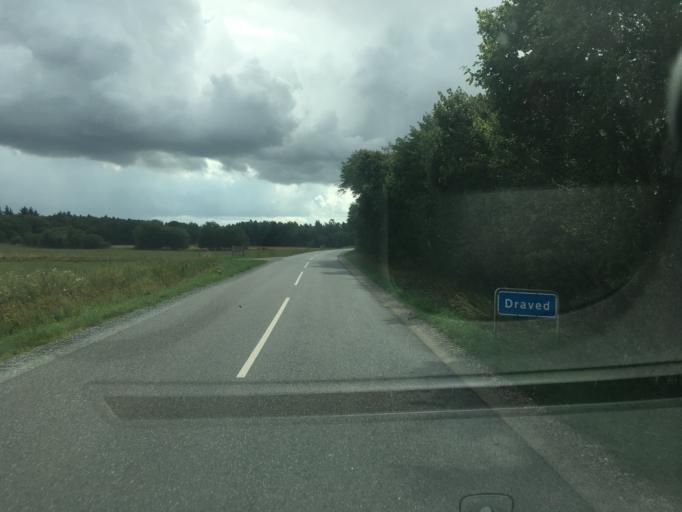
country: DK
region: South Denmark
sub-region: Tonder Kommune
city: Logumkloster
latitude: 55.0312
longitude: 8.9683
